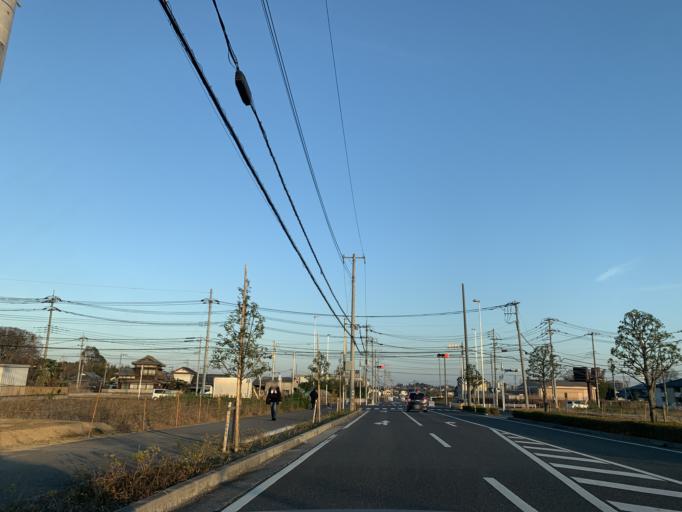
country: JP
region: Chiba
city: Kashiwa
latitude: 35.8725
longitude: 139.9382
